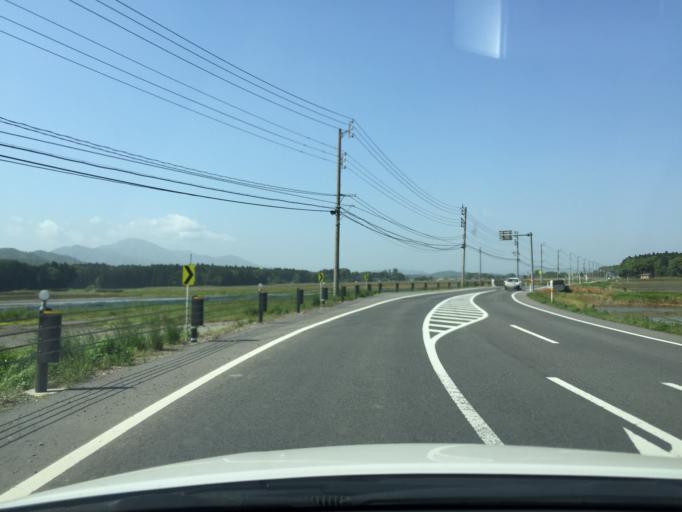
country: JP
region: Niigata
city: Gosen
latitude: 37.7227
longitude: 139.2307
